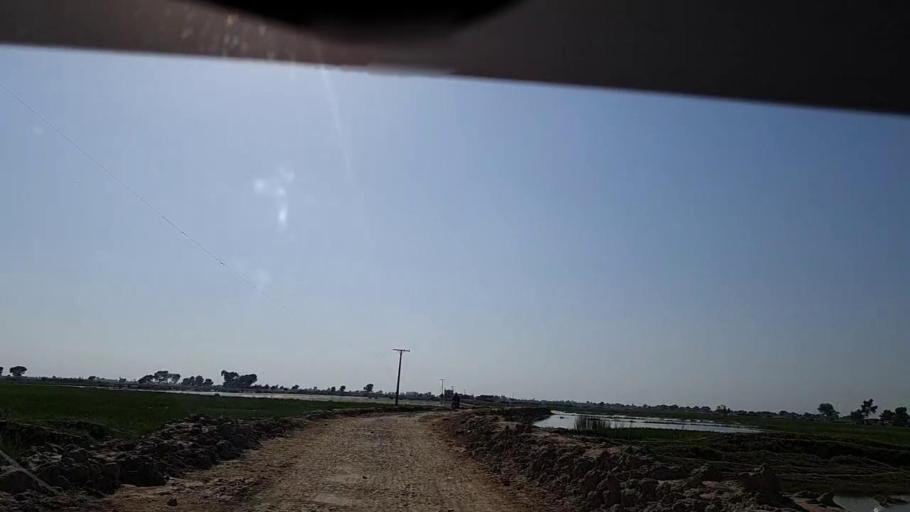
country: PK
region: Sindh
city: Tangwani
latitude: 28.3620
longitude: 69.0182
